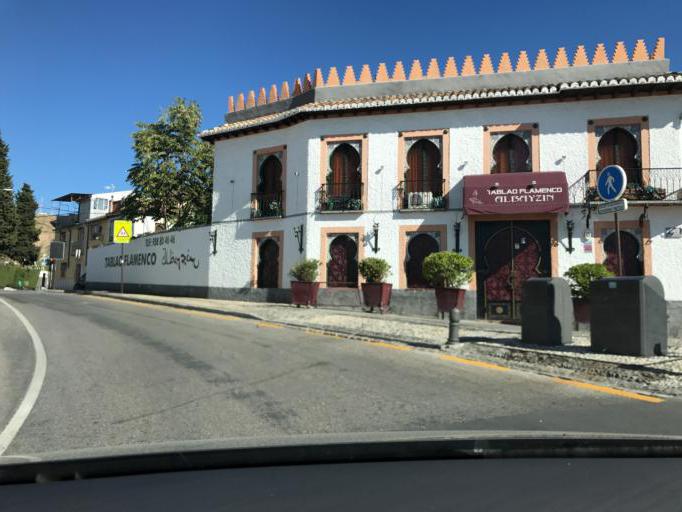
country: ES
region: Andalusia
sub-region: Provincia de Granada
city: Granada
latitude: 37.1832
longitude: -3.5961
